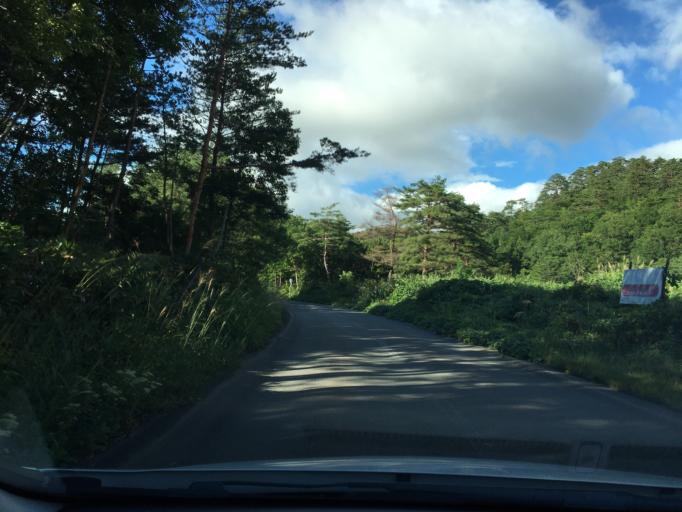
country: JP
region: Yamagata
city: Yonezawa
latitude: 37.8911
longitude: 140.1932
